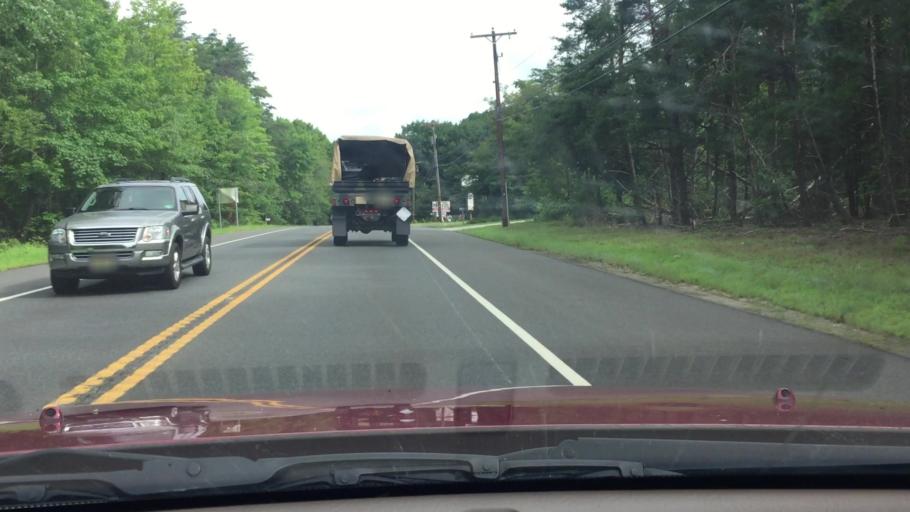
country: US
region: New Jersey
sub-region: Burlington County
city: Fort Dix
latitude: 40.0329
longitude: -74.6422
